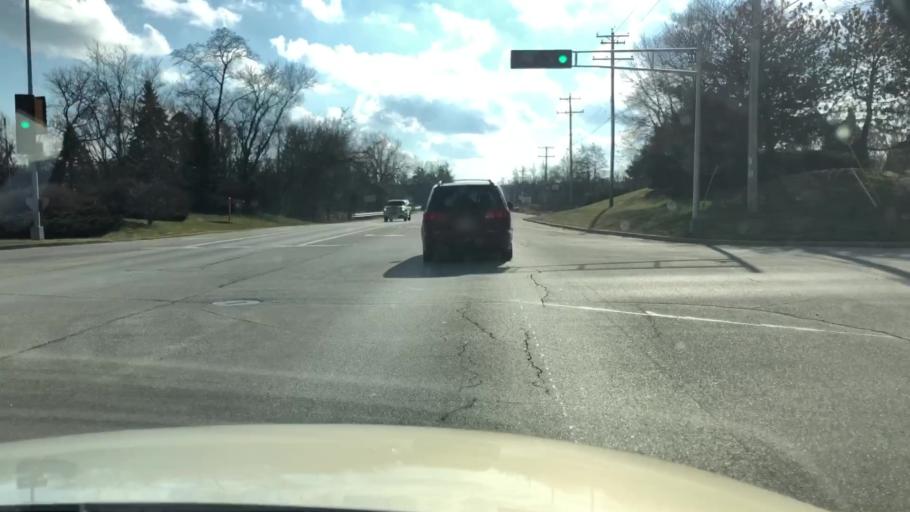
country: US
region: Wisconsin
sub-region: Waukesha County
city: Waukesha
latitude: 43.0576
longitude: -88.1859
